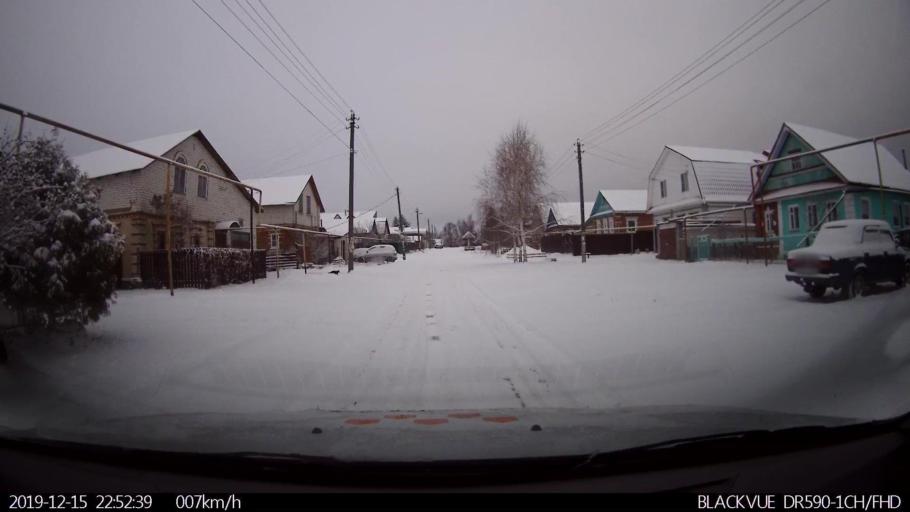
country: RU
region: Nizjnij Novgorod
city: Afonino
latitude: 56.2191
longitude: 44.1140
